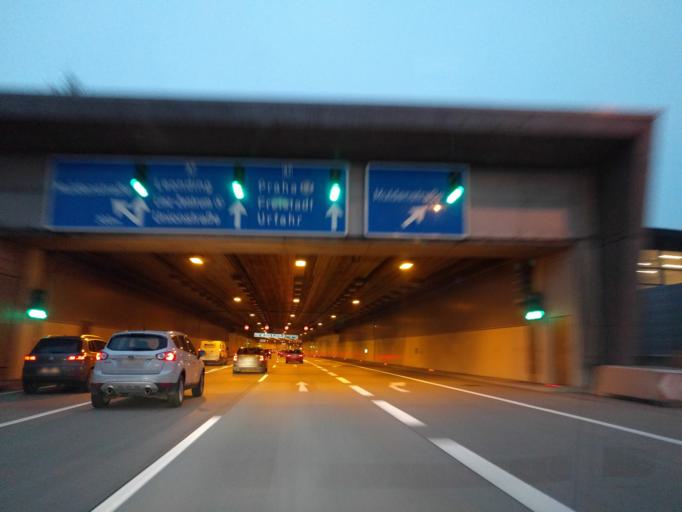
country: AT
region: Upper Austria
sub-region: Linz Stadt
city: Linz
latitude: 48.2666
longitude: 14.2975
